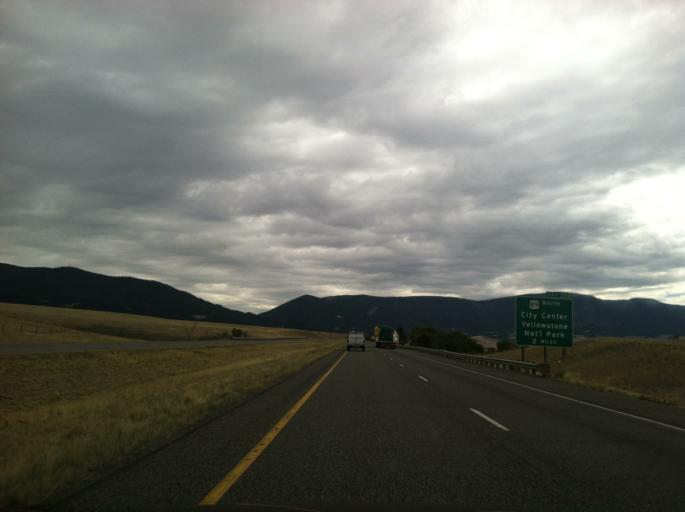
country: US
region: Montana
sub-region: Park County
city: Livingston
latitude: 45.6581
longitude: -110.5345
